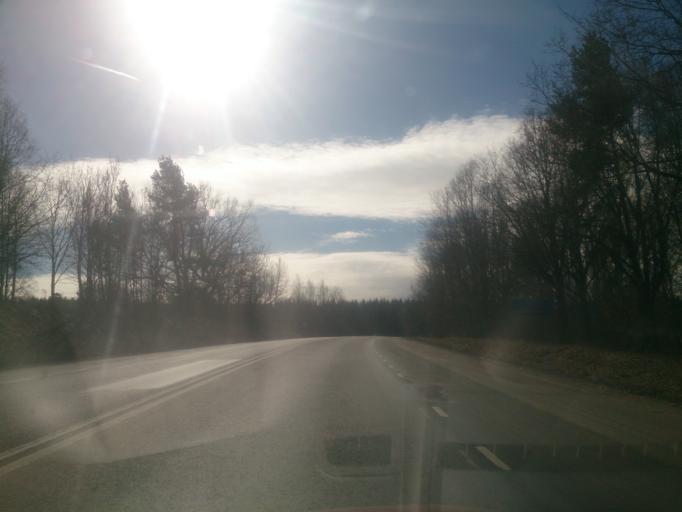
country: SE
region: OEstergoetland
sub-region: Norrkopings Kommun
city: Kimstad
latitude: 58.5073
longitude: 15.9820
